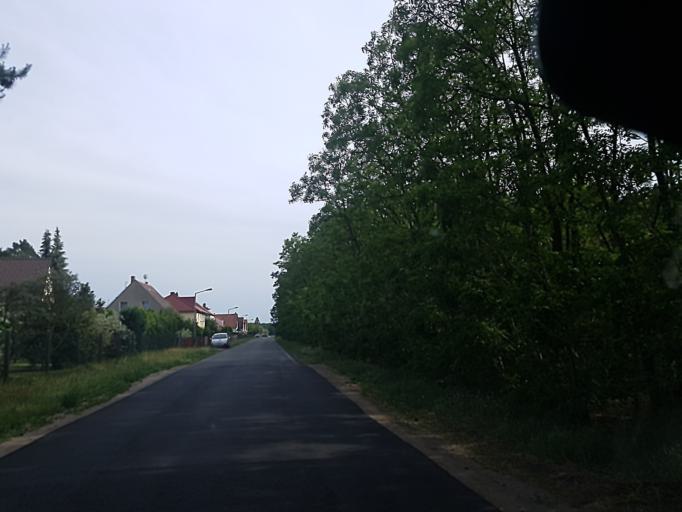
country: DE
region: Saxony-Anhalt
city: Jessen
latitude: 51.8030
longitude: 12.9541
